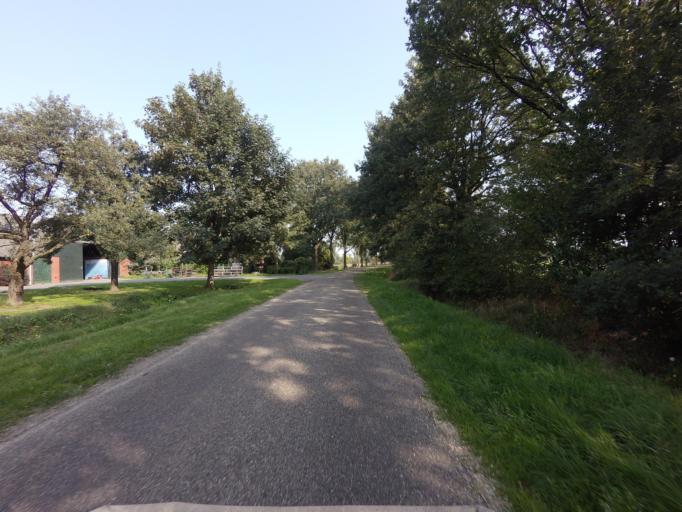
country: NL
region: Drenthe
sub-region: Gemeente Tynaarlo
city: Vries
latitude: 53.1299
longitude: 6.5270
